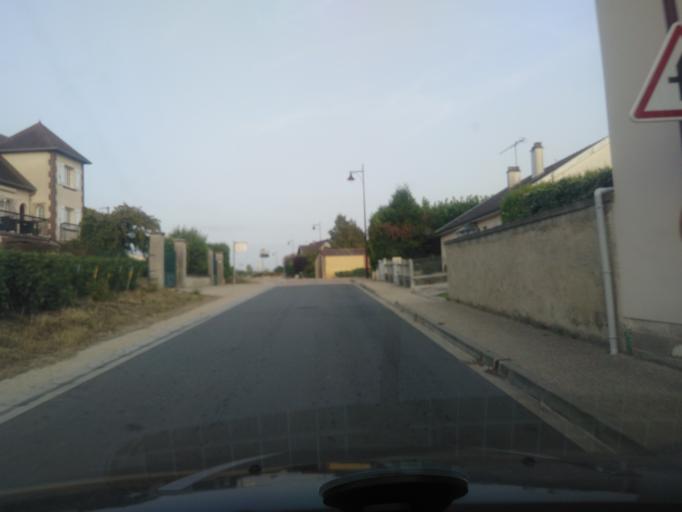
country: FR
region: Champagne-Ardenne
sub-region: Departement de la Marne
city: Damery
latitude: 49.0818
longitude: 3.8440
